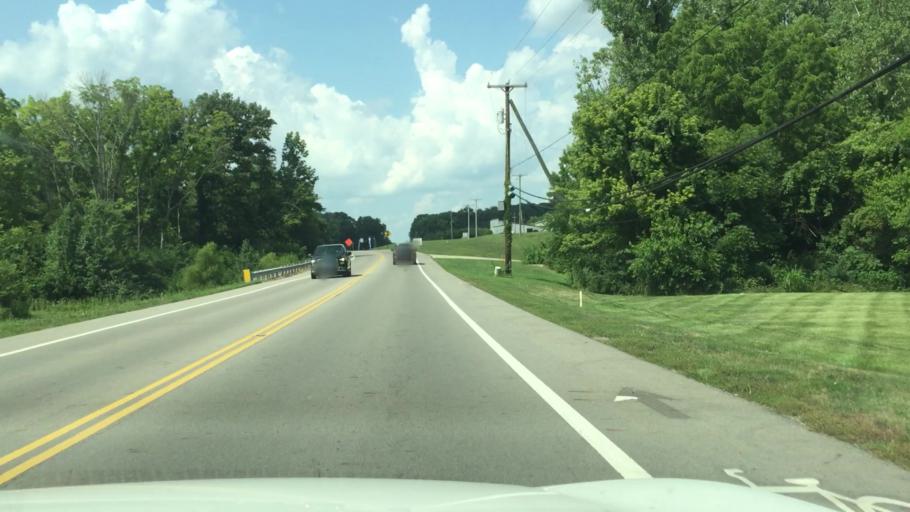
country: US
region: Ohio
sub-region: Clark County
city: Northridge
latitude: 39.9761
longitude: -83.7841
